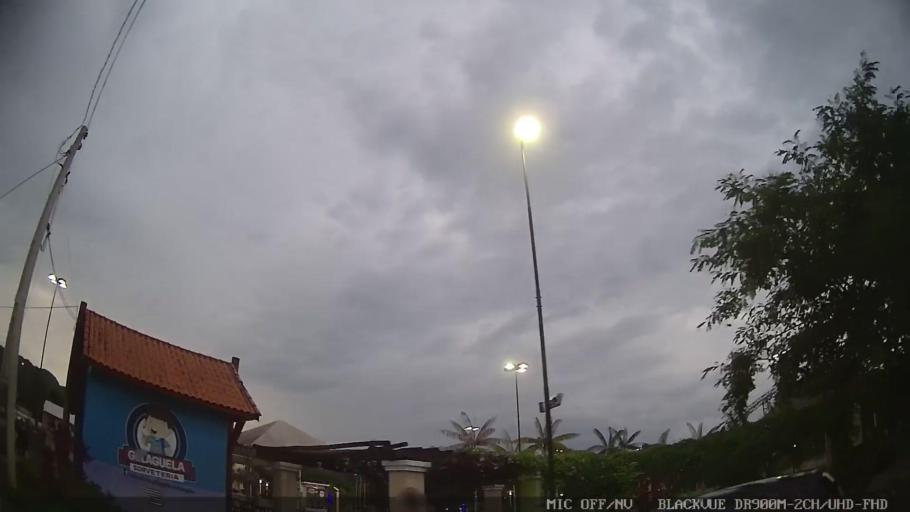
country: BR
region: Sao Paulo
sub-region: Itatiba
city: Itatiba
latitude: -22.8762
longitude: -46.7906
